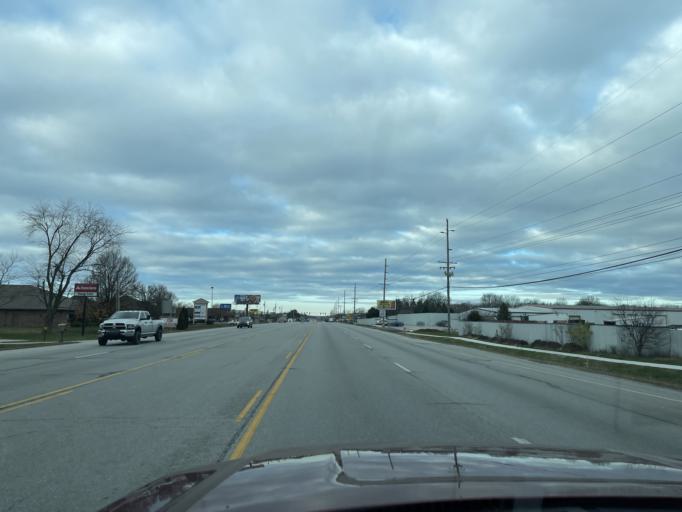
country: US
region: Indiana
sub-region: Hendricks County
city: Avon
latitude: 39.7629
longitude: -86.3907
